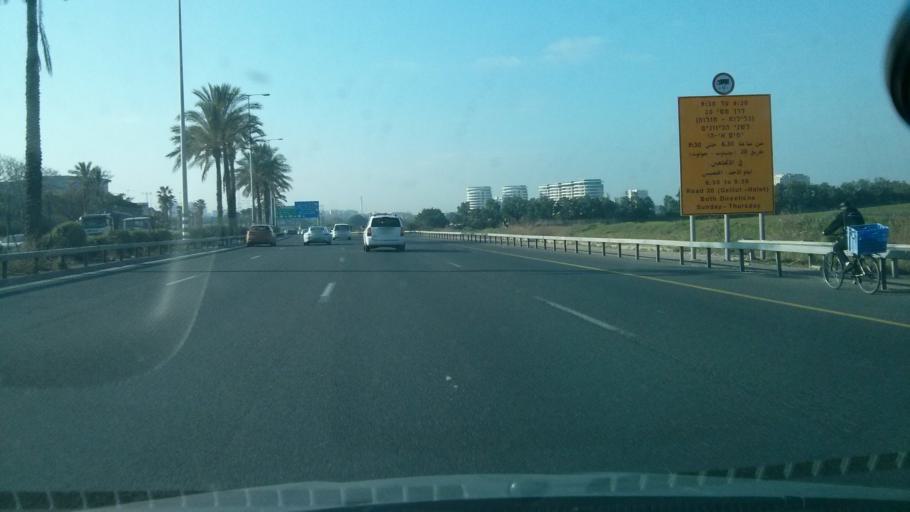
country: IL
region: Tel Aviv
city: Herzliya Pituah
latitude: 32.1505
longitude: 34.8047
